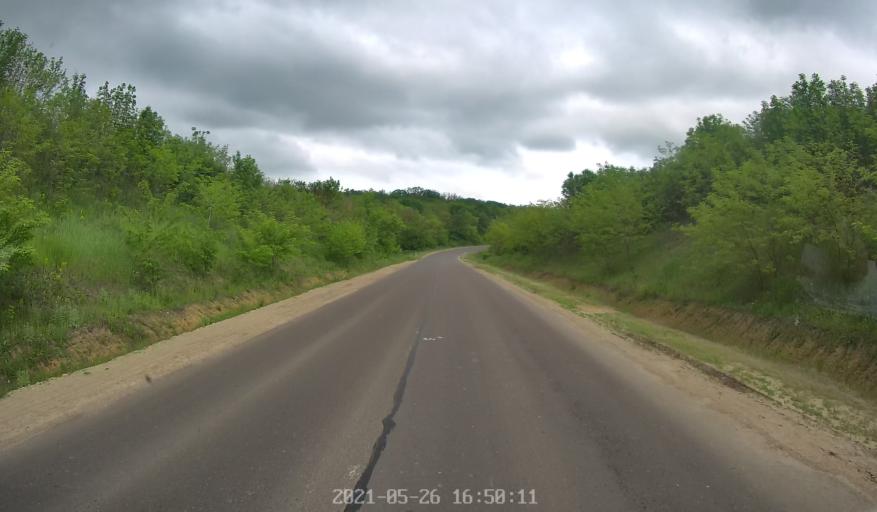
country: MD
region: Hincesti
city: Hincesti
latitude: 46.8693
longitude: 28.4867
